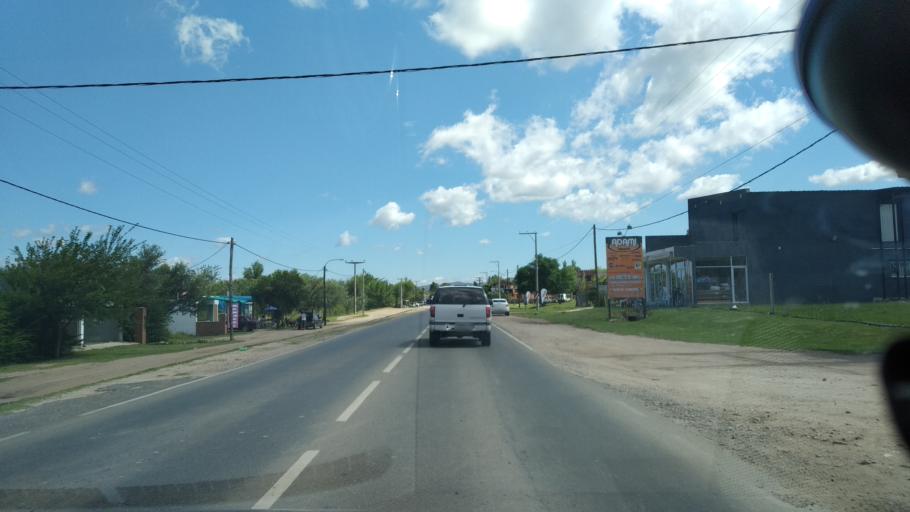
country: AR
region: Cordoba
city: Mina Clavero
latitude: -31.7711
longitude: -65.0007
